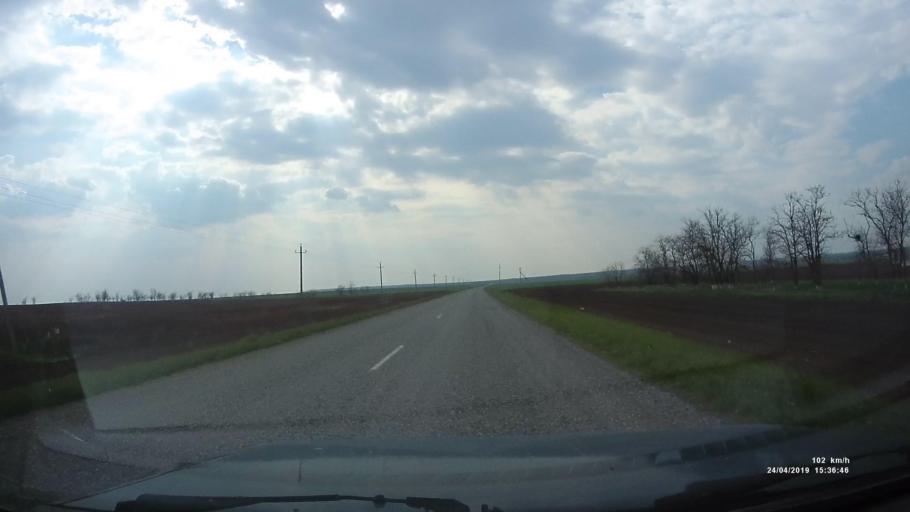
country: RU
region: Kalmykiya
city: Yashalta
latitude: 46.5992
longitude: 42.8635
